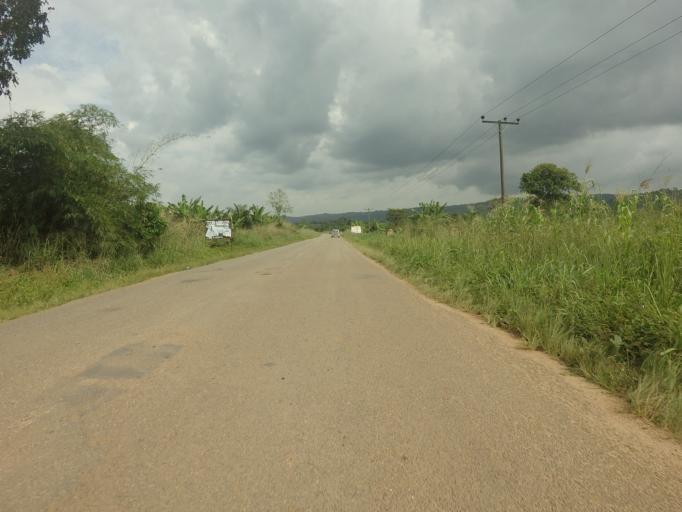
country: GH
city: Akropong
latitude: 5.9552
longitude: -0.1583
